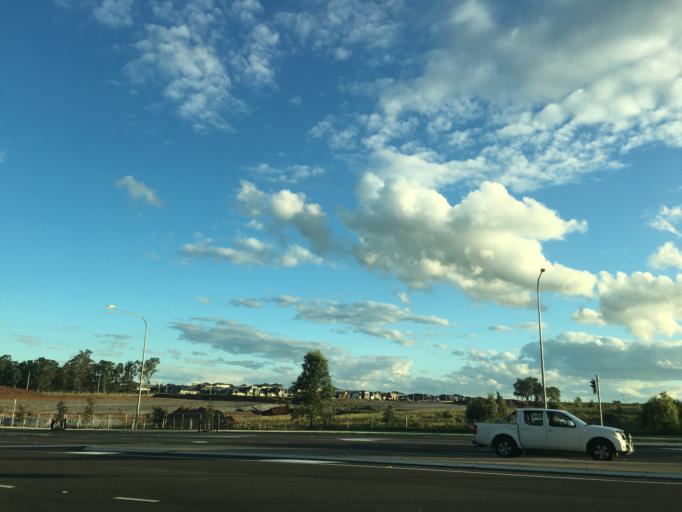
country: AU
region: New South Wales
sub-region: Campbelltown Municipality
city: Denham Court
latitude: -33.9822
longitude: 150.7995
